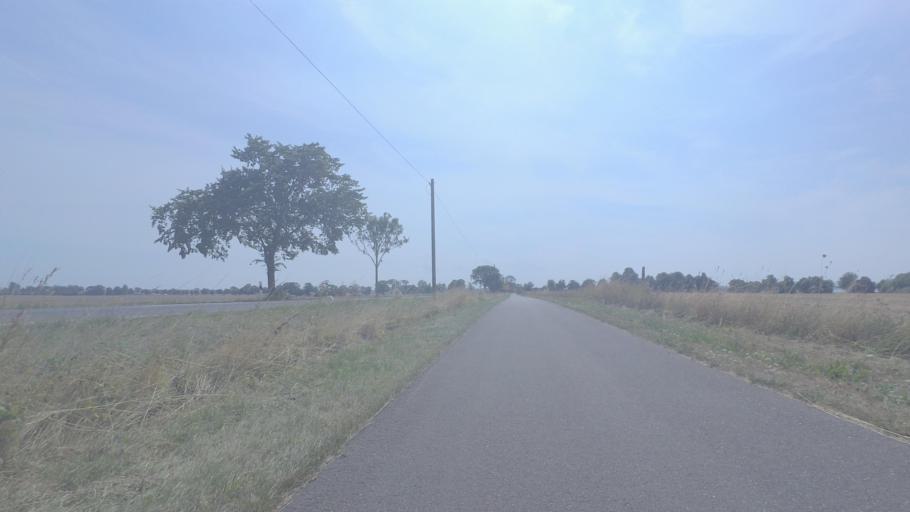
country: DE
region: Mecklenburg-Vorpommern
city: Garz
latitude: 54.2828
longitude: 13.3475
